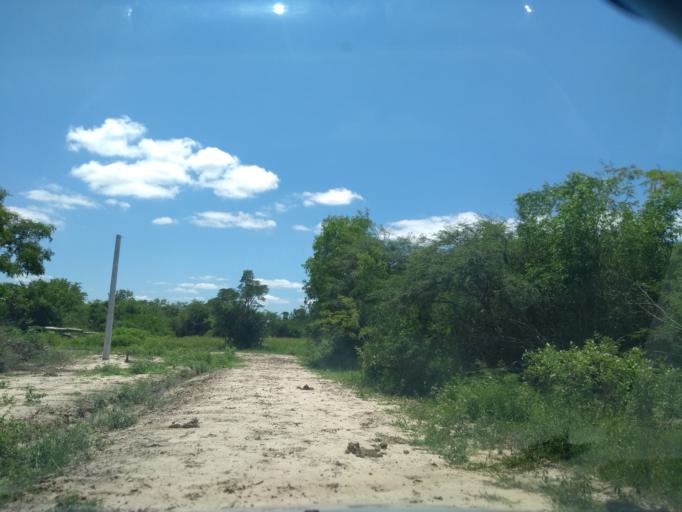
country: AR
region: Chaco
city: Fontana
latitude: -27.4033
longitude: -58.9740
